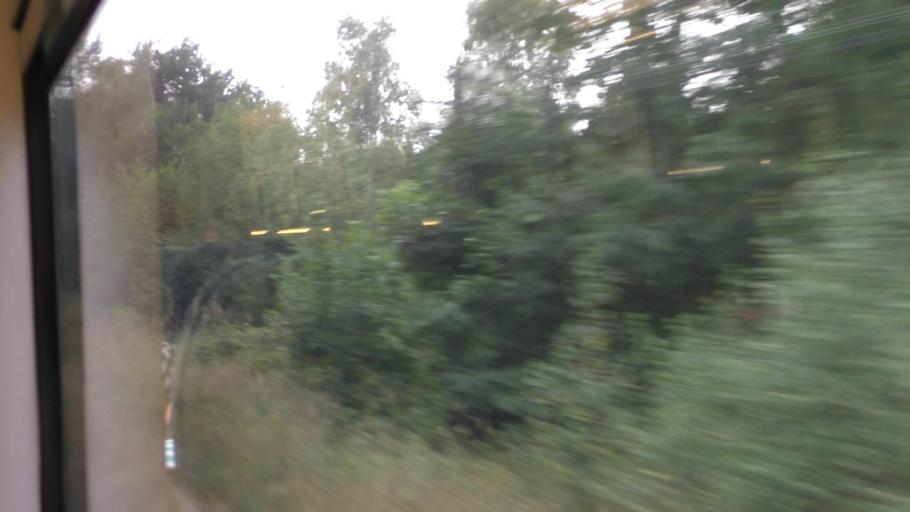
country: DE
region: Saxony
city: Kodersdorf
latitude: 51.2520
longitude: 14.9205
